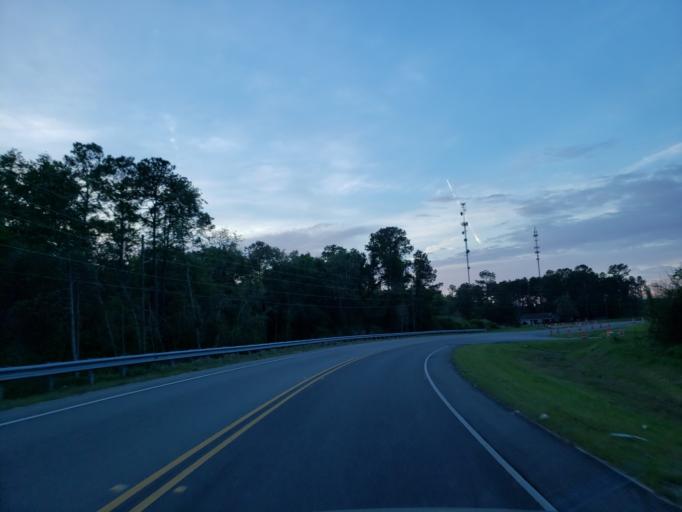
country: US
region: Georgia
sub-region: Lowndes County
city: Hahira
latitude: 30.9912
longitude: -83.3913
